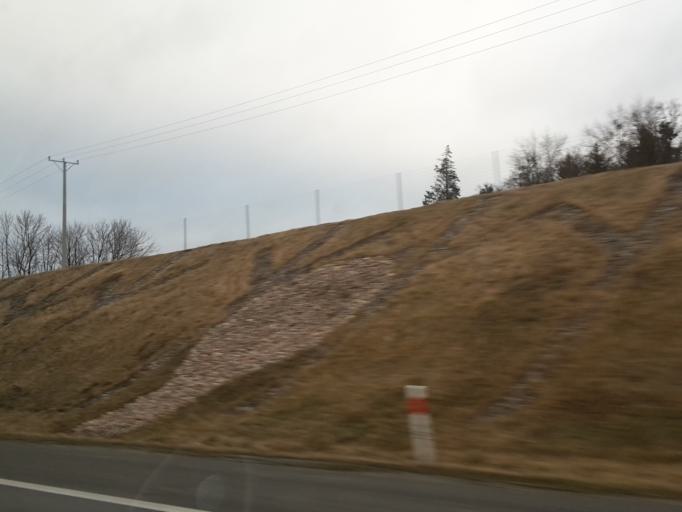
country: PL
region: Warmian-Masurian Voivodeship
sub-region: Powiat ostrodzki
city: Maldyty
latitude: 53.8591
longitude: 19.7493
